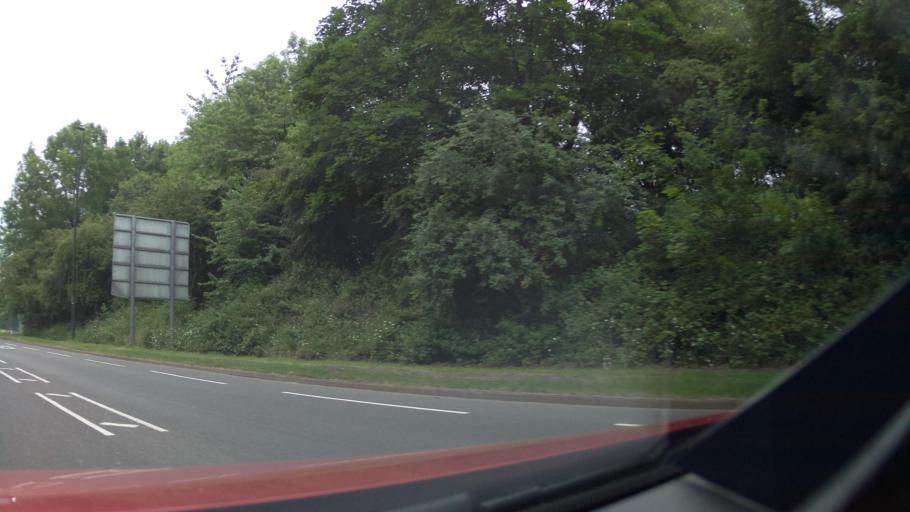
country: GB
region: England
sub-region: Derbyshire
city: Swadlincote
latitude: 52.7681
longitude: -1.5930
